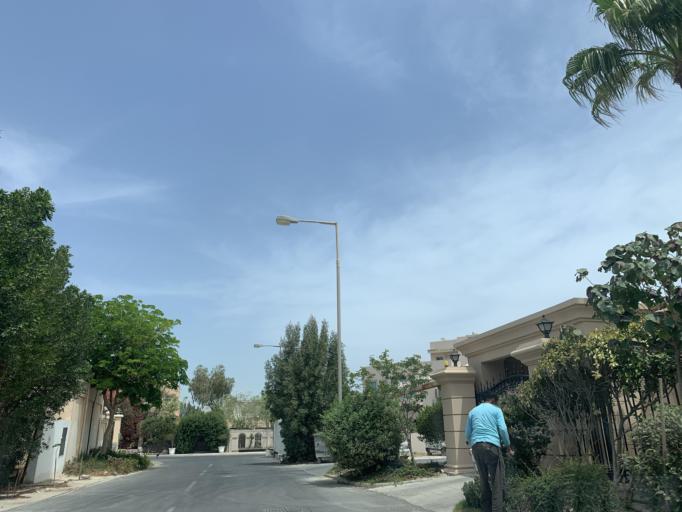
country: BH
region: Northern
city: Ar Rifa'
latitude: 26.1461
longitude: 50.5576
